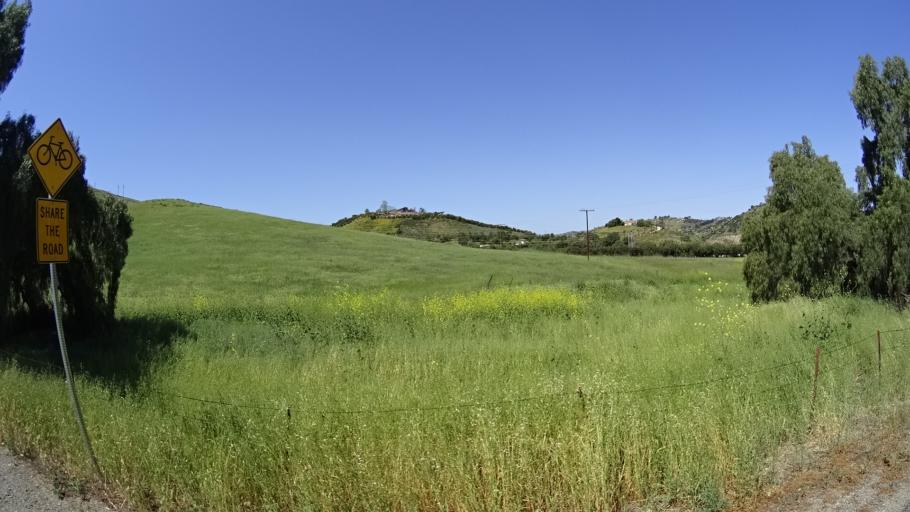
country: US
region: California
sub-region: Ventura County
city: Moorpark
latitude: 34.2424
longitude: -118.8631
